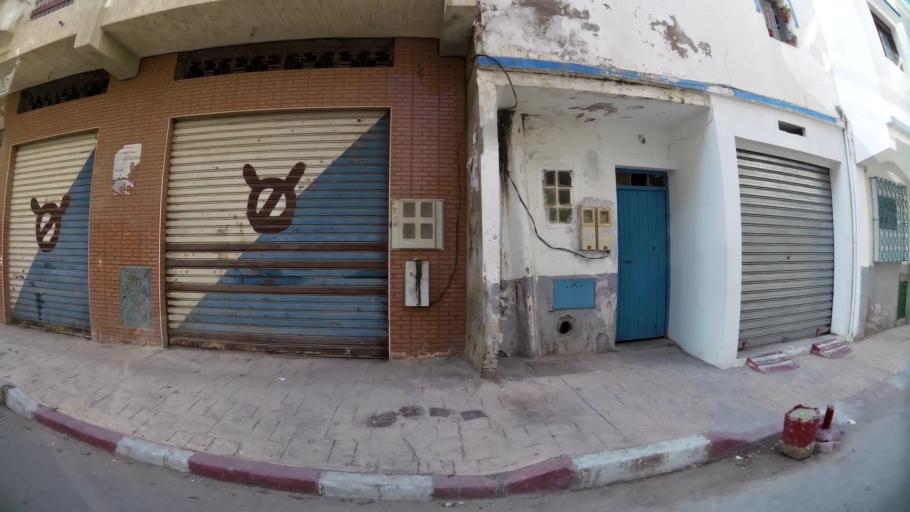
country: MA
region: Tanger-Tetouan
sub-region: Tetouan
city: Martil
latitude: 35.6186
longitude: -5.2776
